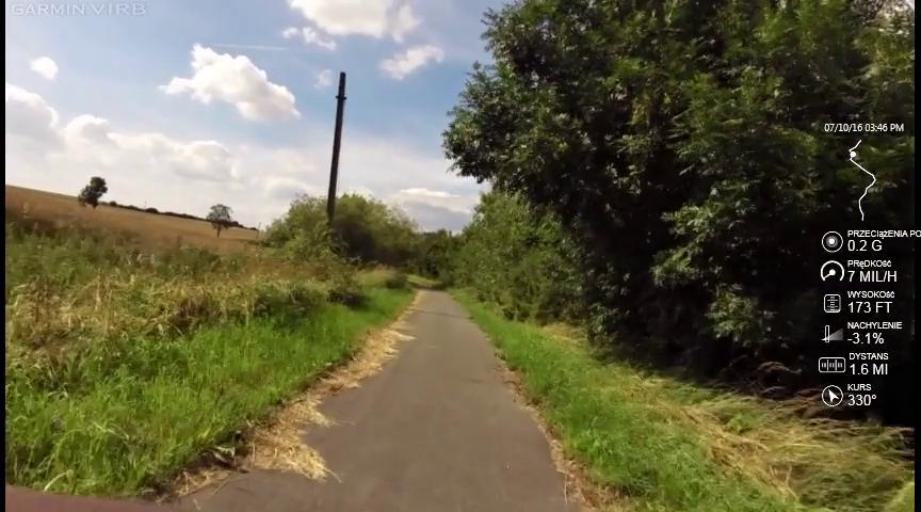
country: PL
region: West Pomeranian Voivodeship
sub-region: Powiat gryfinski
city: Banie
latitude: 53.1336
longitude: 14.6177
